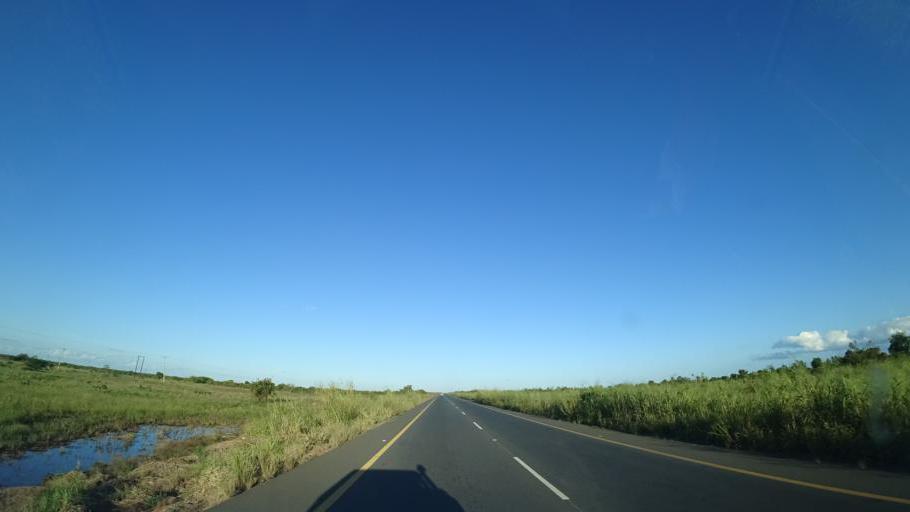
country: MZ
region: Sofala
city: Dondo
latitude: -19.3214
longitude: 34.2951
